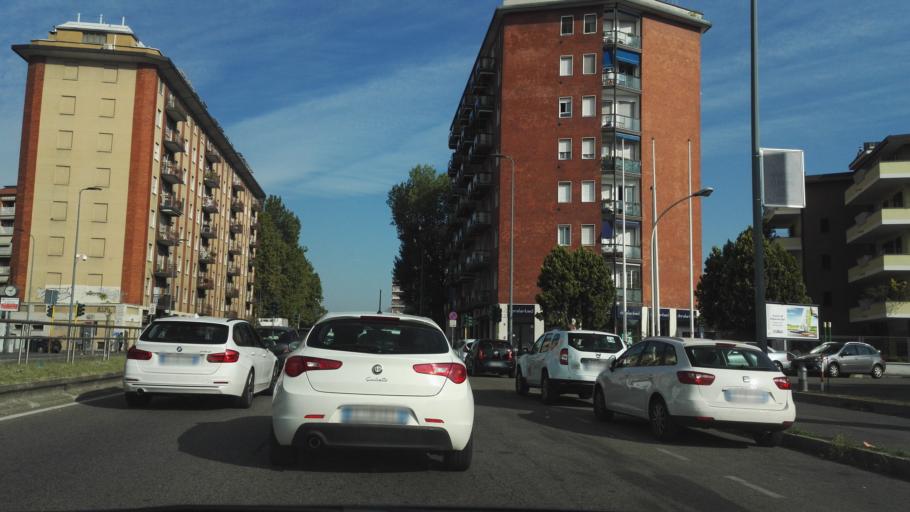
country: IT
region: Lombardy
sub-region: Citta metropolitana di Milano
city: Romano Banco
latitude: 45.4392
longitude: 9.1524
